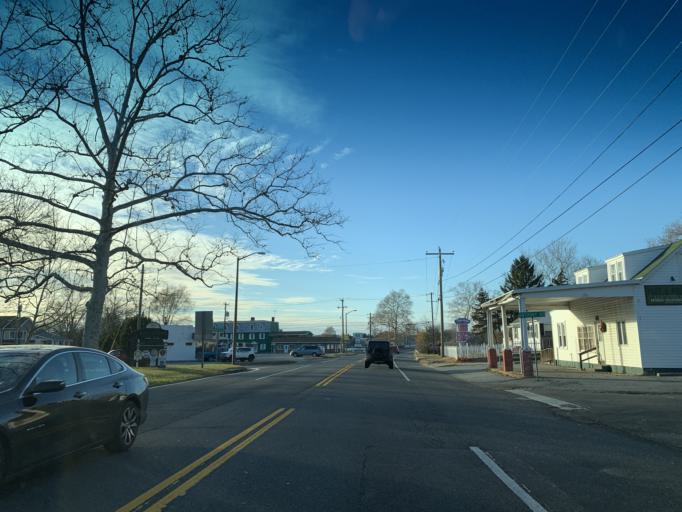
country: US
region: Maryland
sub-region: Queen Anne's County
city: Kingstown
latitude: 39.2058
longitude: -76.0552
